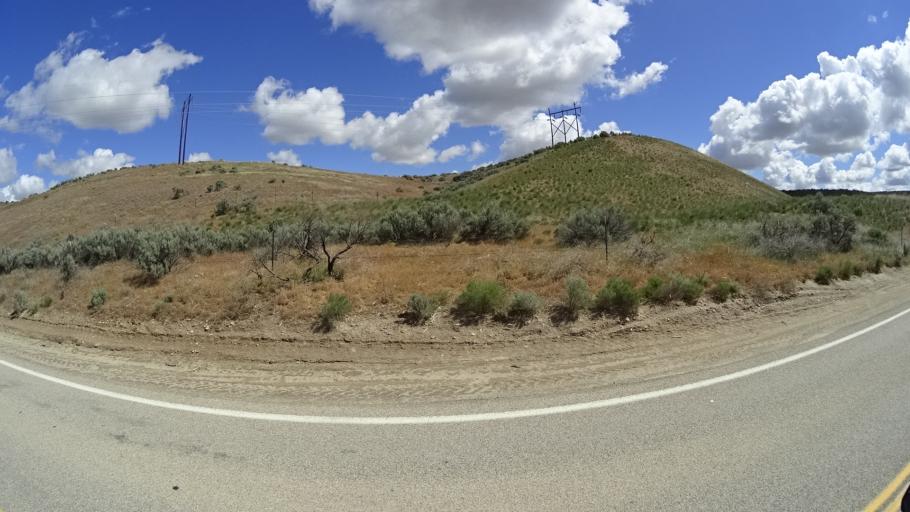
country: US
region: Idaho
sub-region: Ada County
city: Kuna
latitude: 43.5062
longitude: -116.3046
